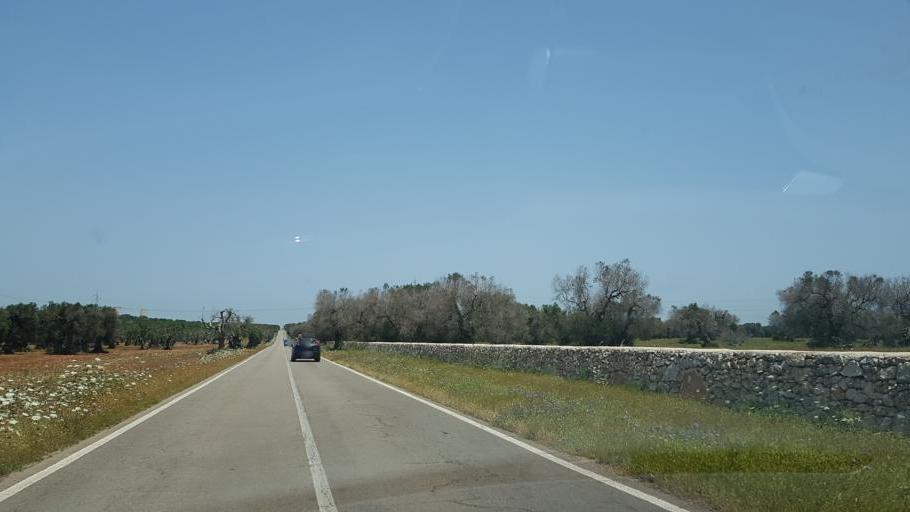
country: IT
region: Apulia
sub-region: Provincia di Lecce
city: Porto Cesareo
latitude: 40.2857
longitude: 17.9099
